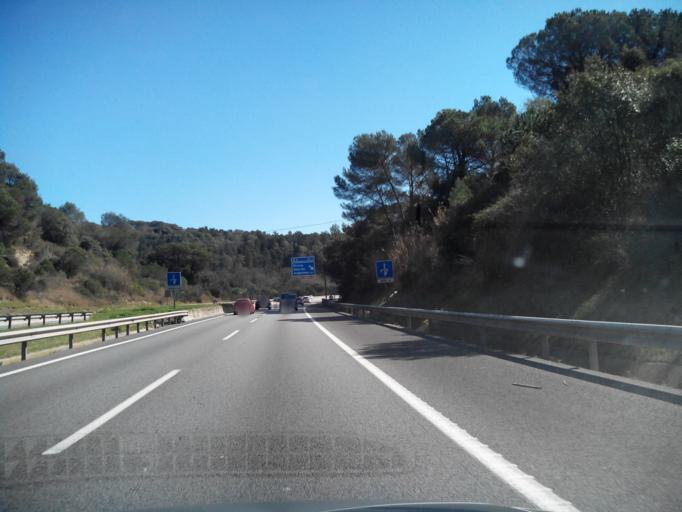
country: ES
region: Catalonia
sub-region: Provincia de Barcelona
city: Argentona
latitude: 41.5796
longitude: 2.3780
